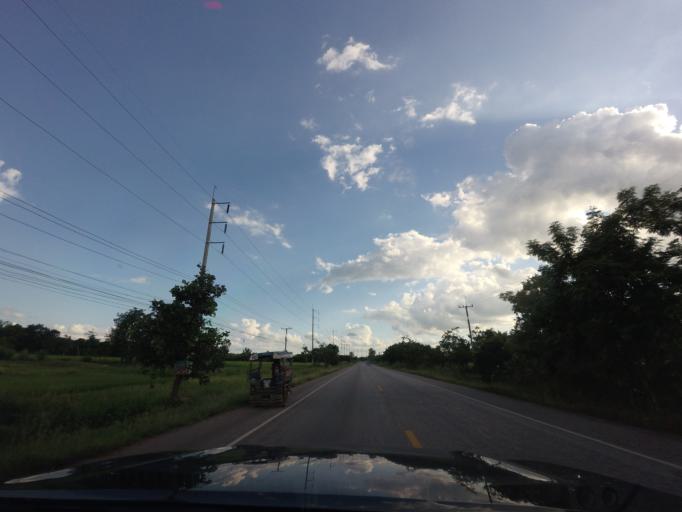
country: TH
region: Changwat Udon Thani
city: Thung Fon
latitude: 17.4726
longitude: 103.1937
